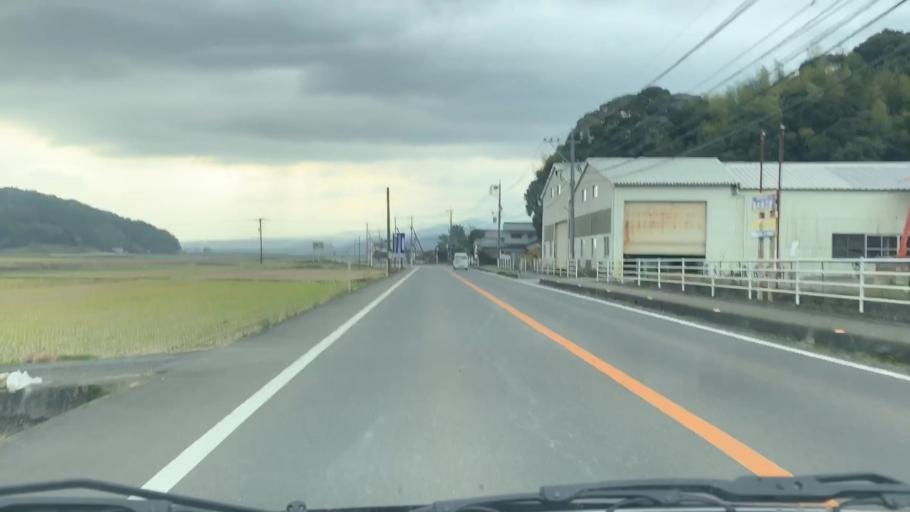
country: JP
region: Saga Prefecture
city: Kashima
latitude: 33.1461
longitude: 130.0630
